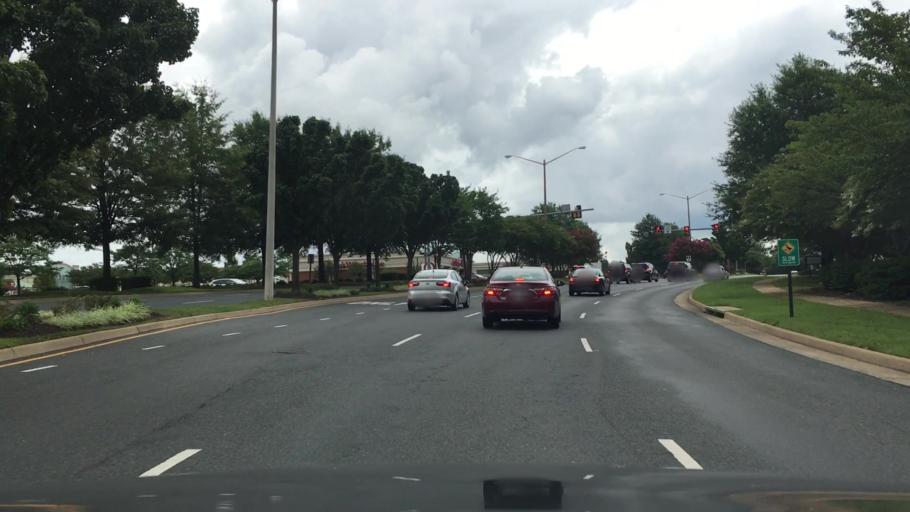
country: US
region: Virginia
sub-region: Stafford County
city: Falmouth
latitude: 38.2986
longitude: -77.5121
